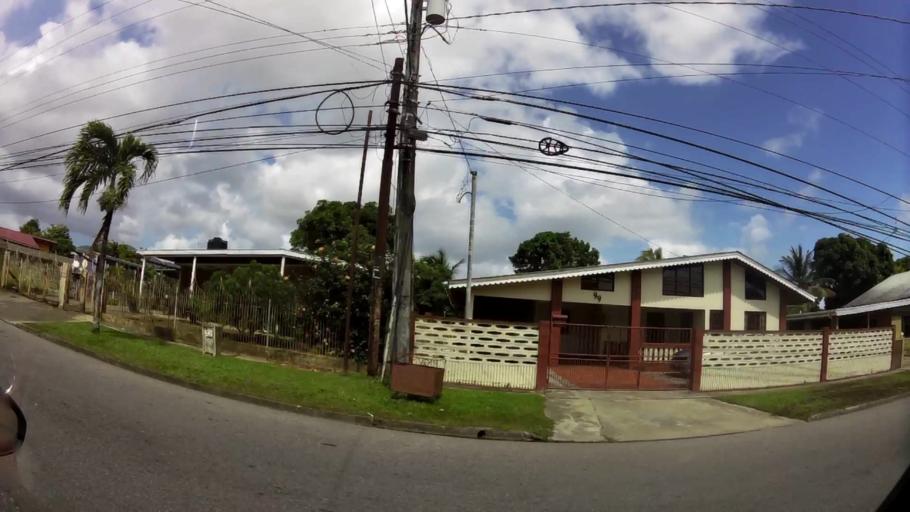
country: TT
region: Borough of Arima
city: Arima
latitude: 10.6236
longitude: -61.2656
